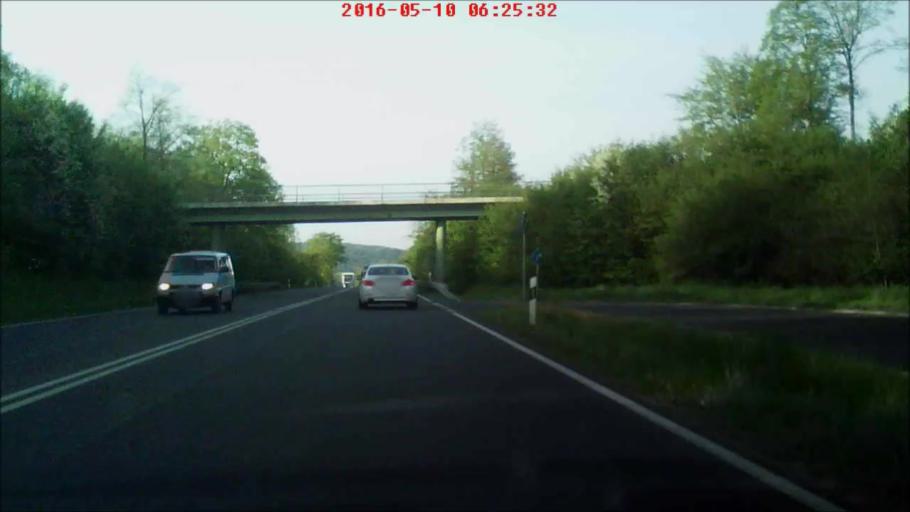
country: DE
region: Hesse
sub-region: Regierungsbezirk Kassel
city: Hunfeld
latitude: 50.6564
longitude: 9.7525
